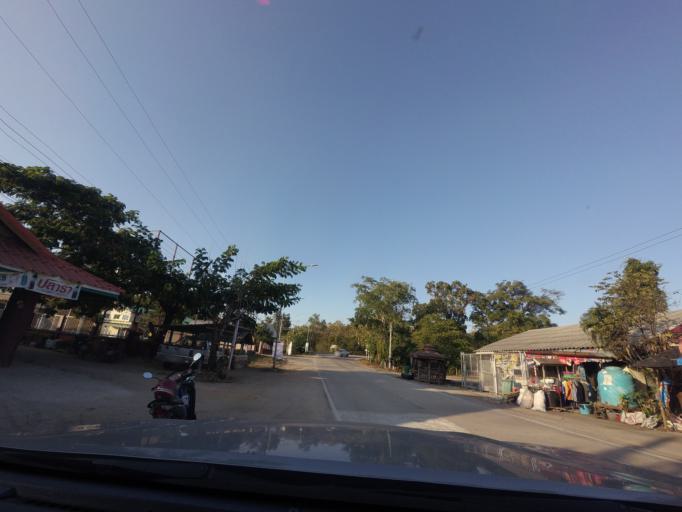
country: TH
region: Lampang
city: Mae Mo
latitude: 18.4181
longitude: 99.7282
